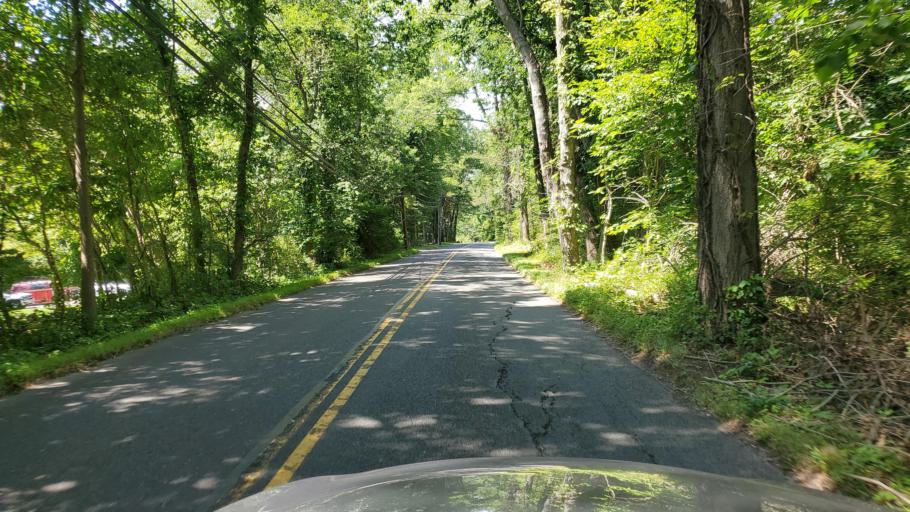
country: US
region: Connecticut
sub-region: Fairfield County
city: Southport
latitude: 41.1699
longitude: -73.2966
